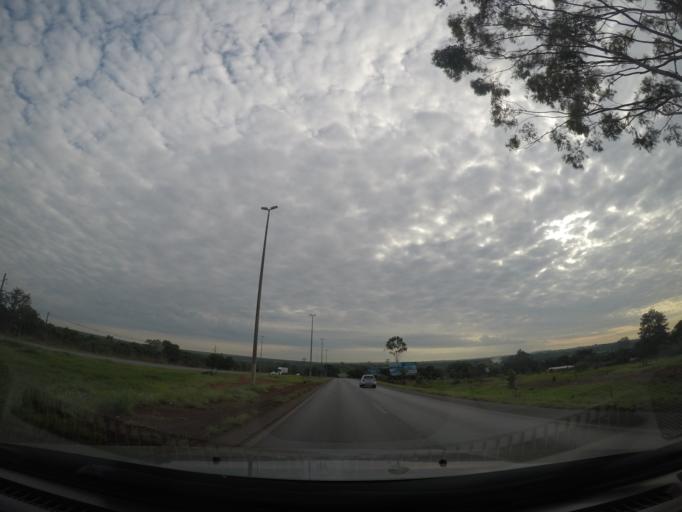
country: BR
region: Goias
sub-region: Planaltina
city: Planaltina
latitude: -15.5971
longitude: -47.6731
